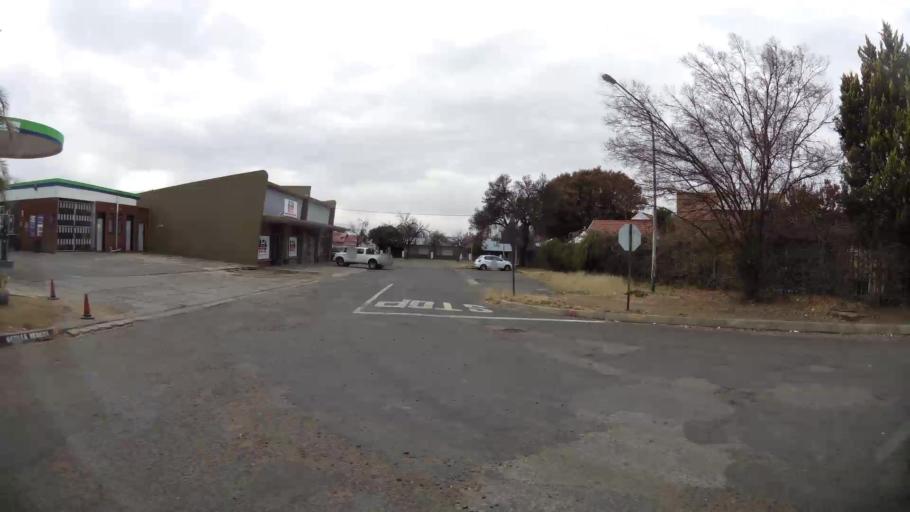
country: ZA
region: Orange Free State
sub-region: Fezile Dabi District Municipality
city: Kroonstad
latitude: -27.6466
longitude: 27.2342
